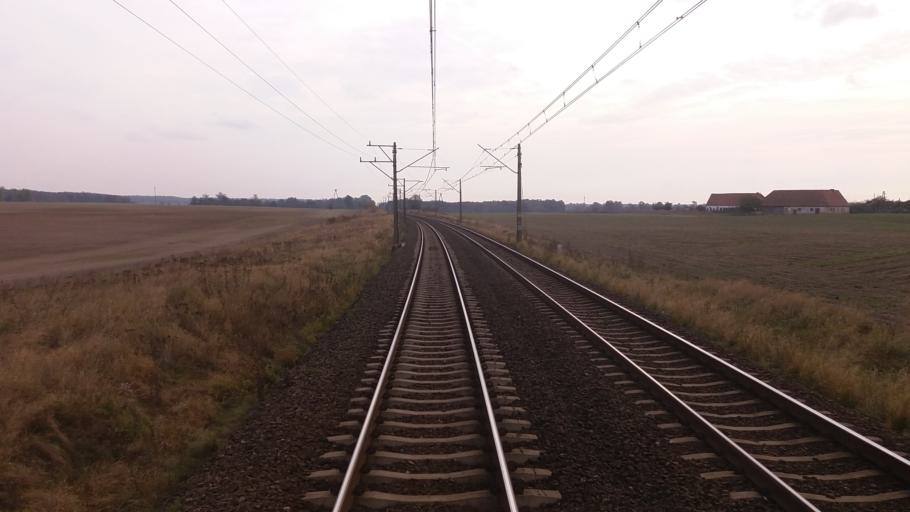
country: PL
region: West Pomeranian Voivodeship
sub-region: Powiat stargardzki
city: Dolice
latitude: 53.2312
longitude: 15.1368
